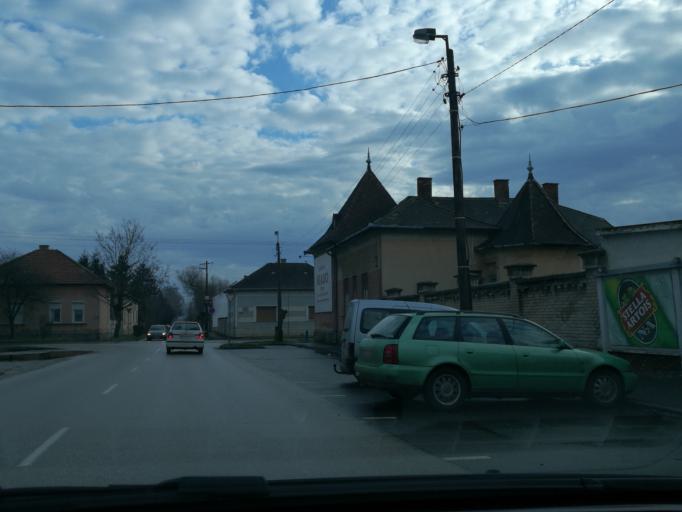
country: HU
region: Szabolcs-Szatmar-Bereg
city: Nyiregyhaza
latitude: 47.9495
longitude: 21.7318
